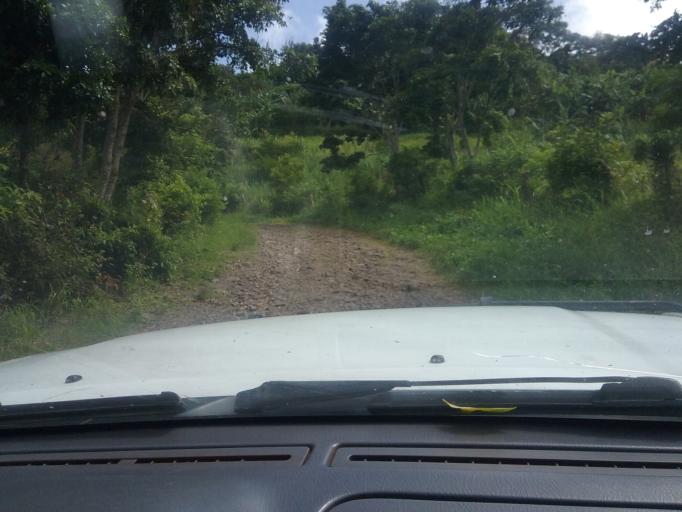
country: NI
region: Matagalpa
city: Matagalpa
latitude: 12.8639
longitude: -85.9094
